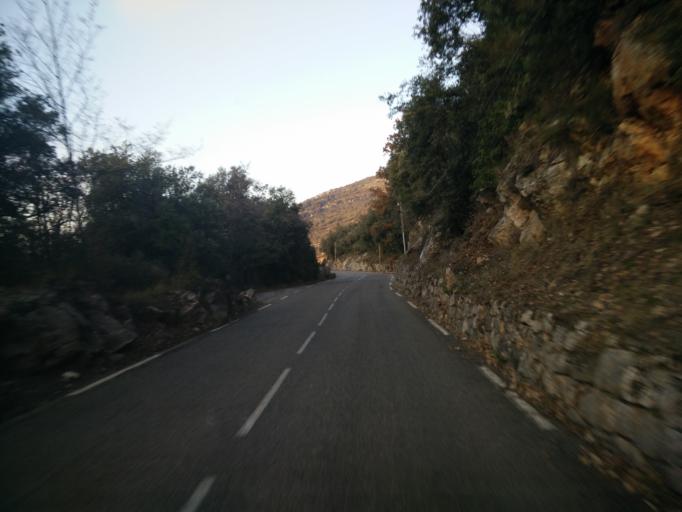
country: FR
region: Provence-Alpes-Cote d'Azur
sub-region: Departement des Alpes-Maritimes
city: Peillon
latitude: 43.7820
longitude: 7.4037
